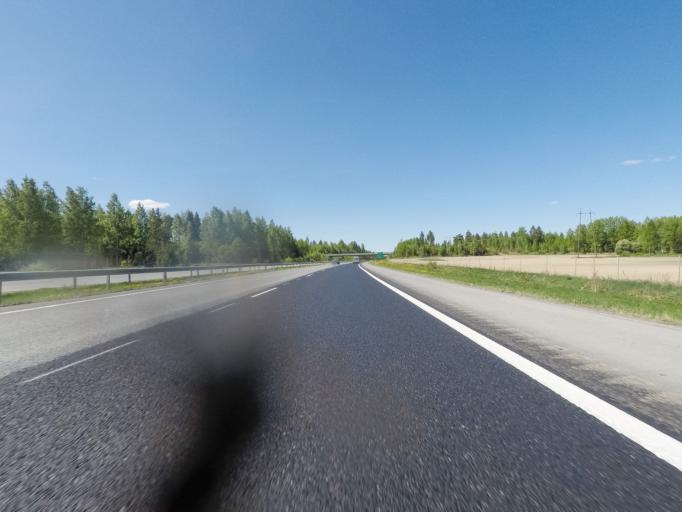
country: FI
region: Pirkanmaa
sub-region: Etelae-Pirkanmaa
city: Akaa
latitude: 61.1949
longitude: 23.8559
